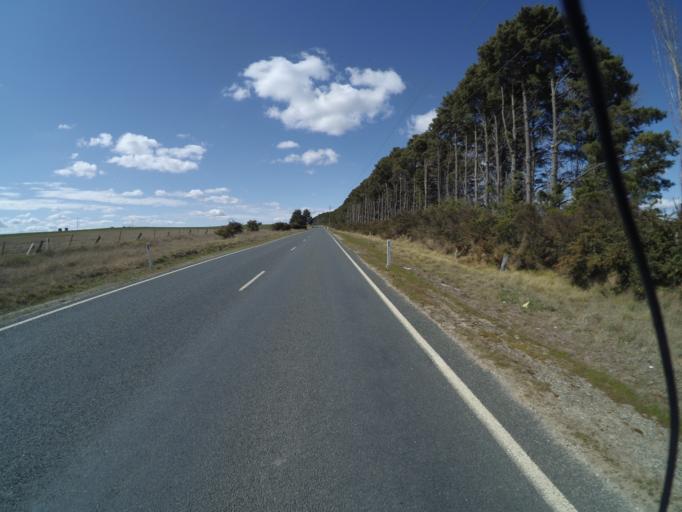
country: AU
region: New South Wales
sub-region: Palerang
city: Bungendore
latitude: -35.2236
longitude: 149.4573
